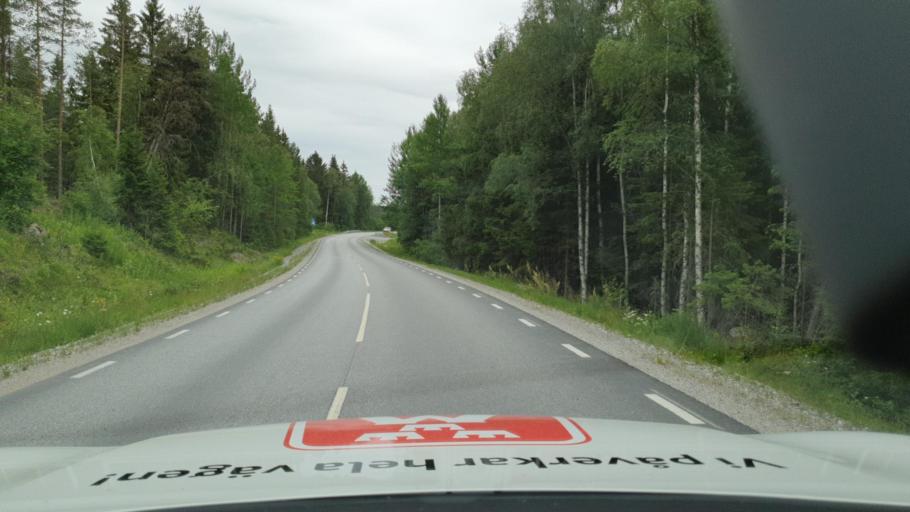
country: SE
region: Vaesterbotten
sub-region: Nordmalings Kommun
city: Nordmaling
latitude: 63.5695
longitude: 19.4250
